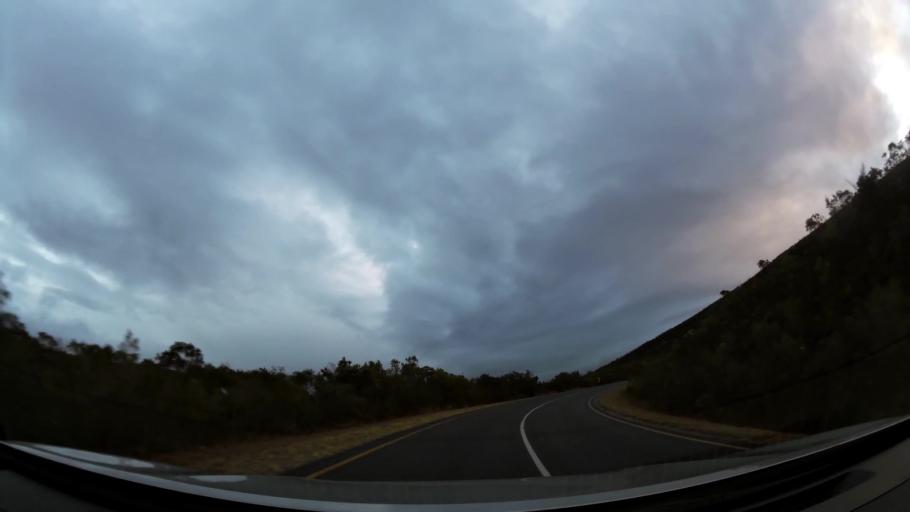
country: ZA
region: Western Cape
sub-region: Overberg District Municipality
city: Swellendam
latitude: -33.9872
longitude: 20.7159
